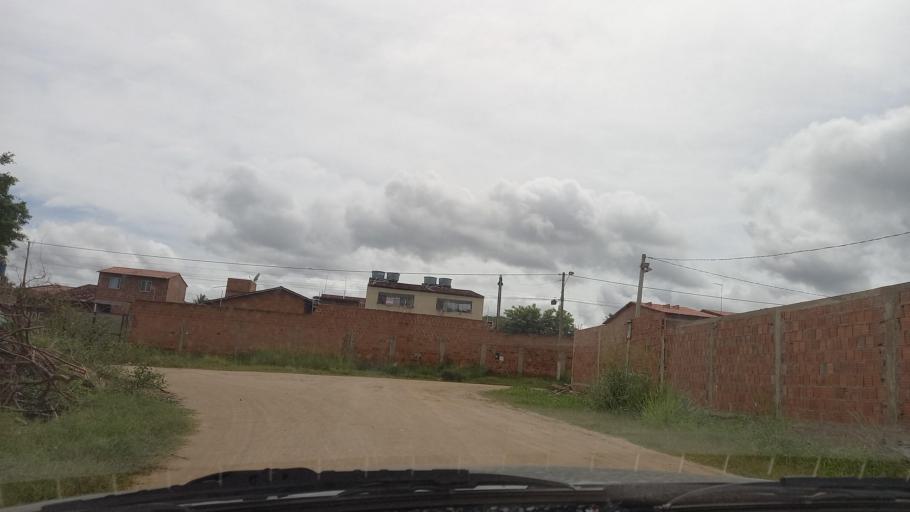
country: ET
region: Oromiya
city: Gore
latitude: 8.1904
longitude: 35.5795
